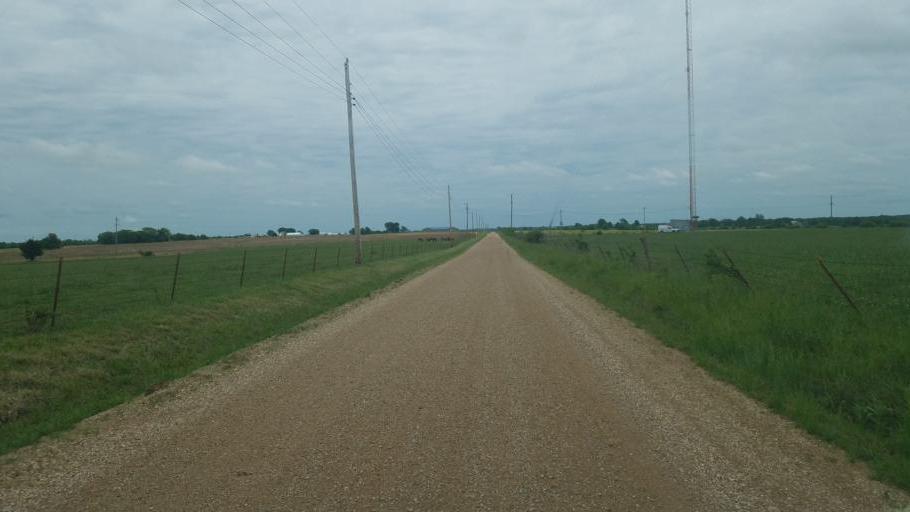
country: US
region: Missouri
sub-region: Morgan County
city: Versailles
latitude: 38.4929
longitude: -92.8024
